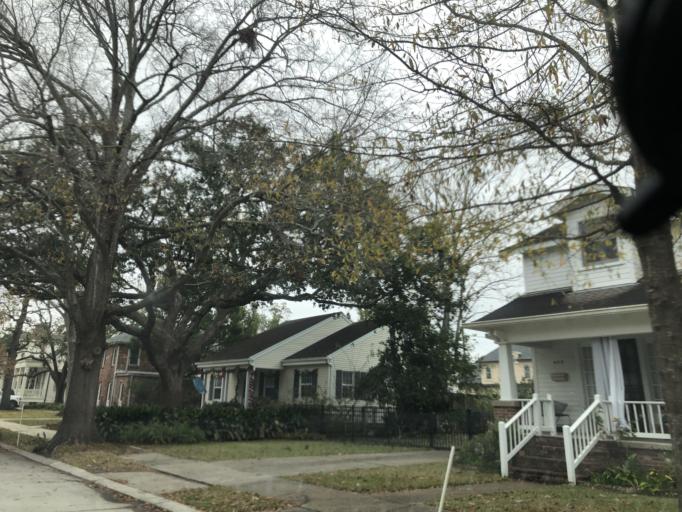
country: US
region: Louisiana
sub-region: Jefferson Parish
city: Metairie
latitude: 29.9787
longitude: -90.1493
